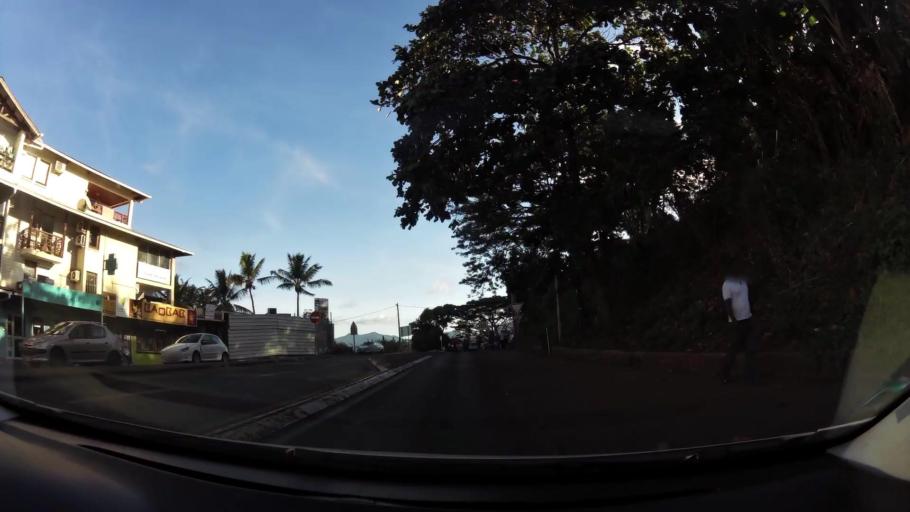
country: YT
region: Mamoudzou
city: Mamoudzou
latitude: -12.7846
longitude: 45.2289
